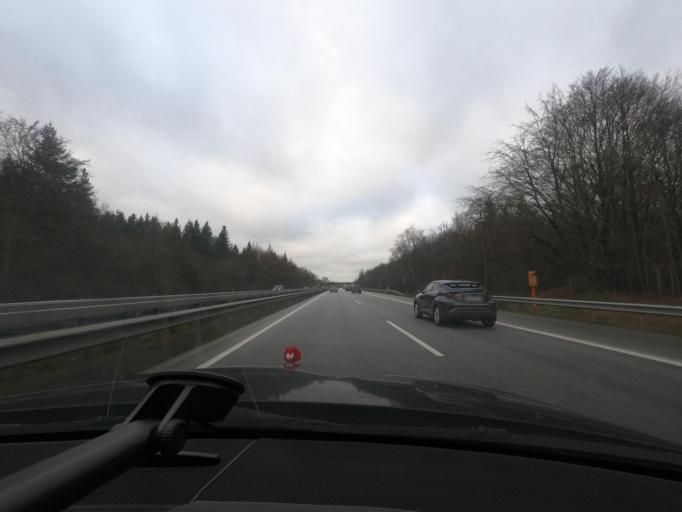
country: DE
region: Schleswig-Holstein
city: Gross Vollstedt
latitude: 54.2347
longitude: 9.8290
